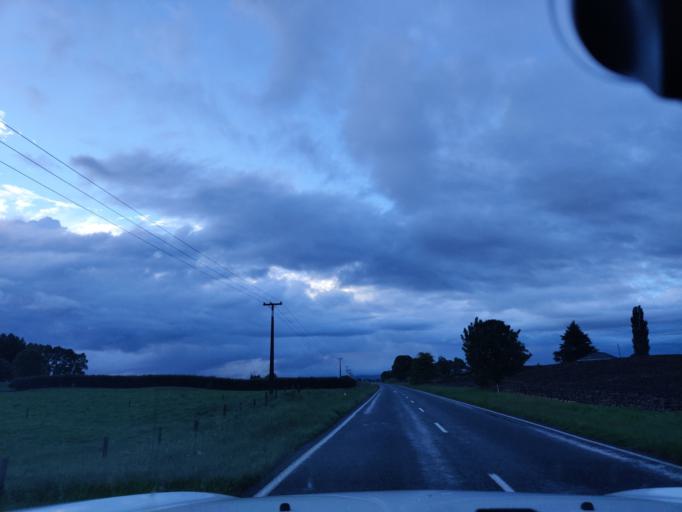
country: NZ
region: Waikato
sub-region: South Waikato District
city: Tokoroa
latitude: -38.2287
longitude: 175.8359
